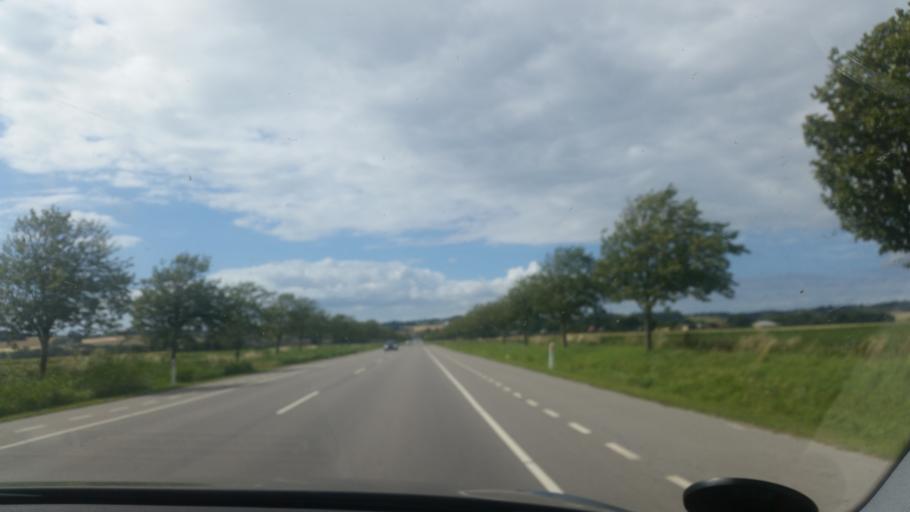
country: DK
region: Zealand
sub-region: Odsherred Kommune
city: Horve
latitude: 55.7944
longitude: 11.4543
